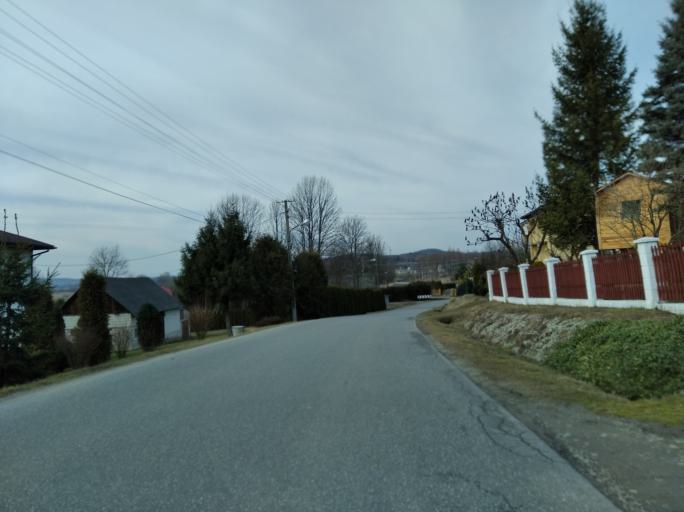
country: PL
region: Subcarpathian Voivodeship
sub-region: Powiat brzozowski
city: Gorki
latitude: 49.6511
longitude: 22.0330
